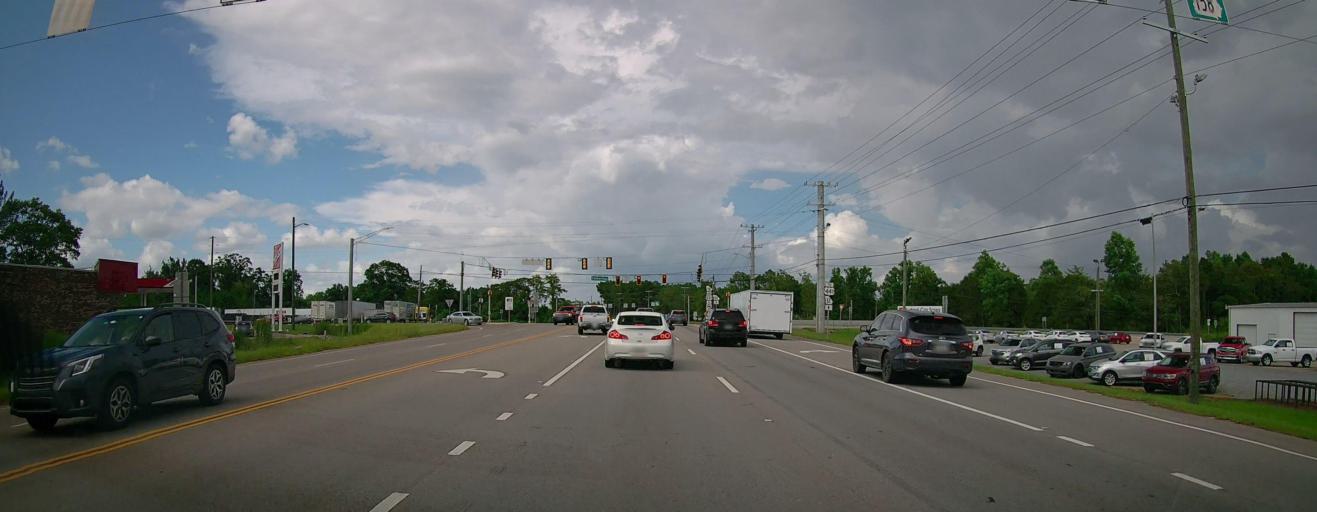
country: US
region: Georgia
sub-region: Coffee County
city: Douglas
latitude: 31.4947
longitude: -82.8302
